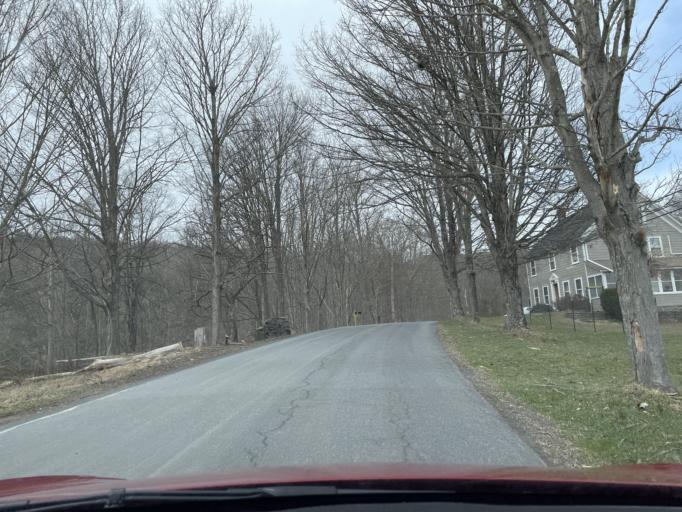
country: US
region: New York
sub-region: Ulster County
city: Saugerties
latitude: 42.1026
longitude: -73.9774
